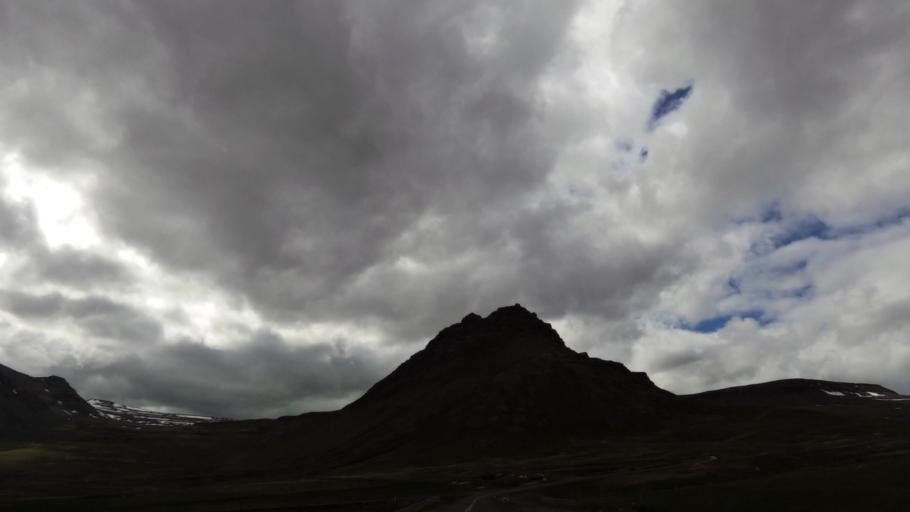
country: IS
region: Westfjords
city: Isafjoerdur
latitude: 66.1581
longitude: -23.2874
